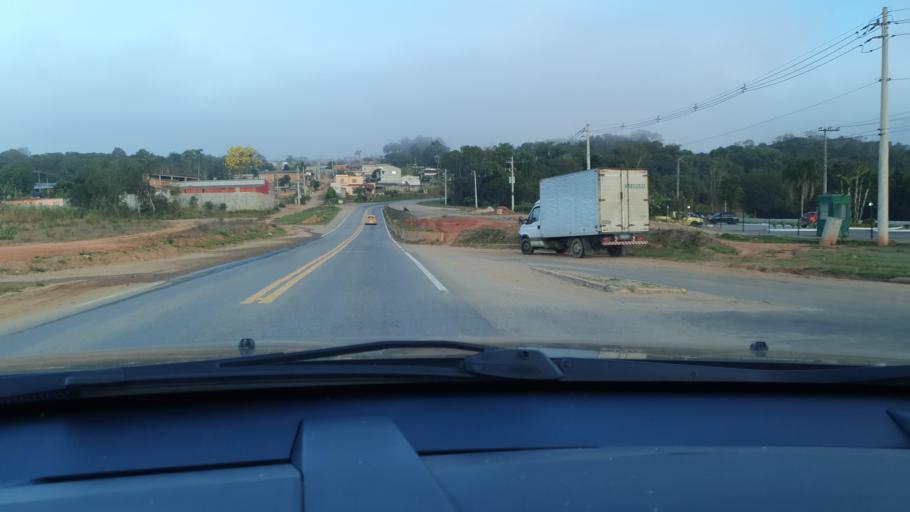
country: BR
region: Sao Paulo
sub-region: Vargem Grande Paulista
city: Vargem Grande Paulista
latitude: -23.6575
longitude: -47.0846
